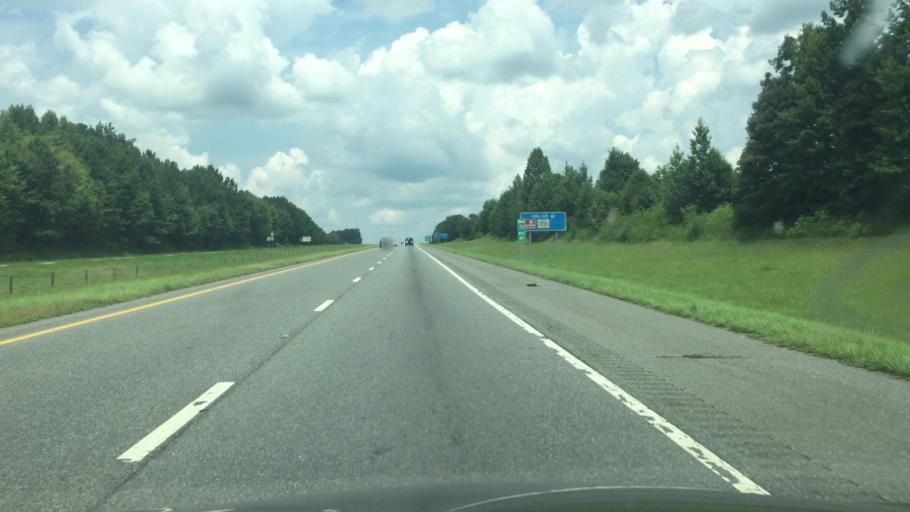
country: US
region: North Carolina
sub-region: Montgomery County
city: Biscoe
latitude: 35.5264
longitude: -79.7856
